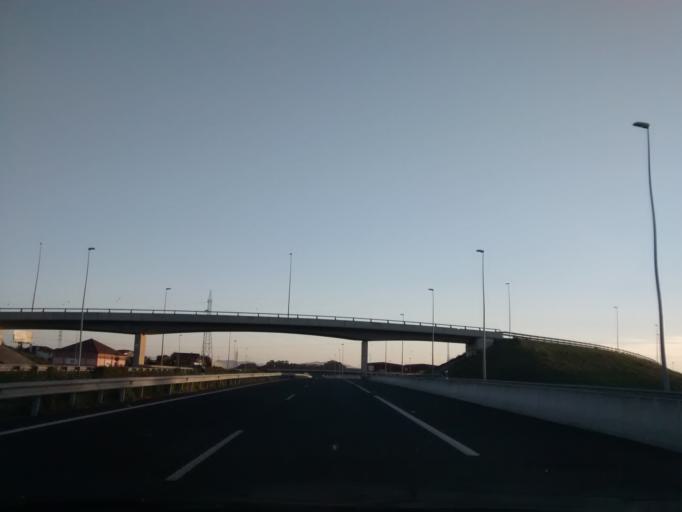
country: ES
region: Cantabria
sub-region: Provincia de Cantabria
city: Santa Cruz de Bezana
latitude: 43.4388
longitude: -3.8761
